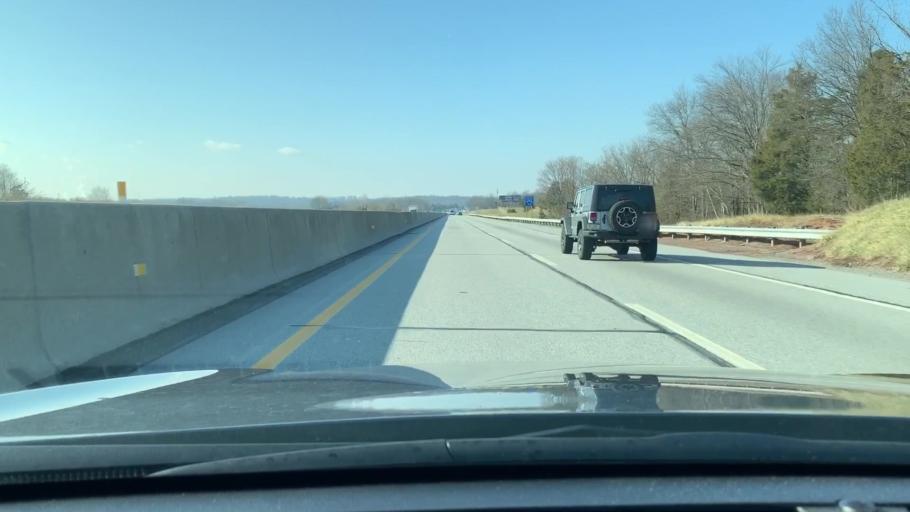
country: US
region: Pennsylvania
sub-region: Lancaster County
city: Elizabethtown
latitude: 40.2075
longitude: -76.5854
